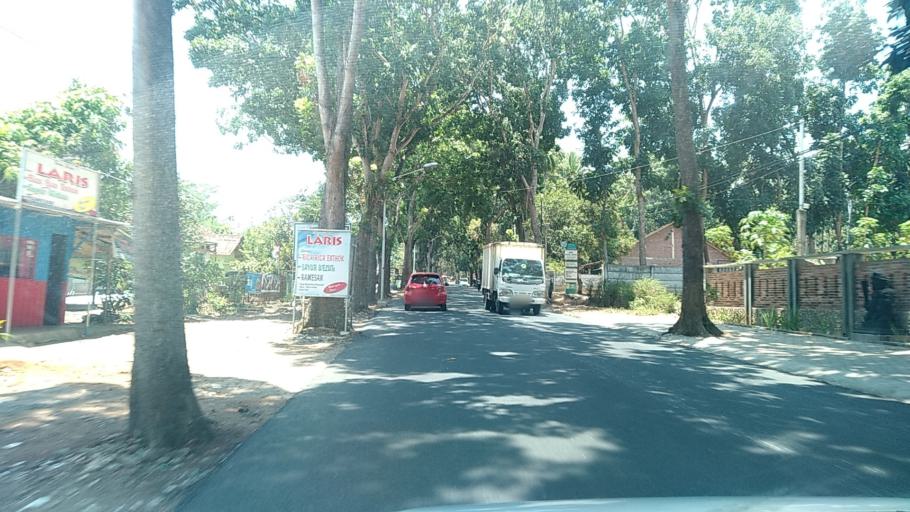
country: ID
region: Central Java
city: Ungaran
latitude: -7.0679
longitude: 110.3590
